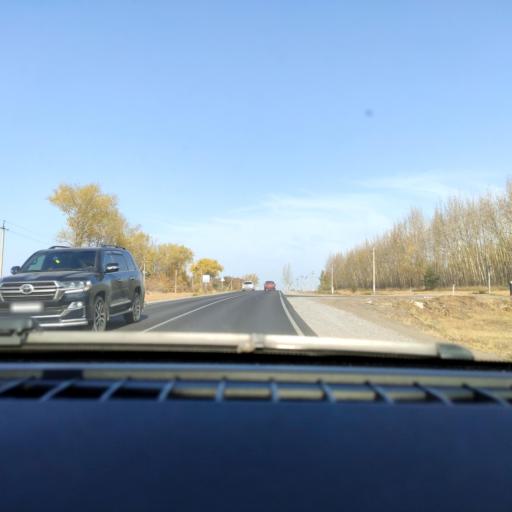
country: RU
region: Voronezj
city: Novaya Usman'
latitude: 51.6821
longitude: 39.3966
